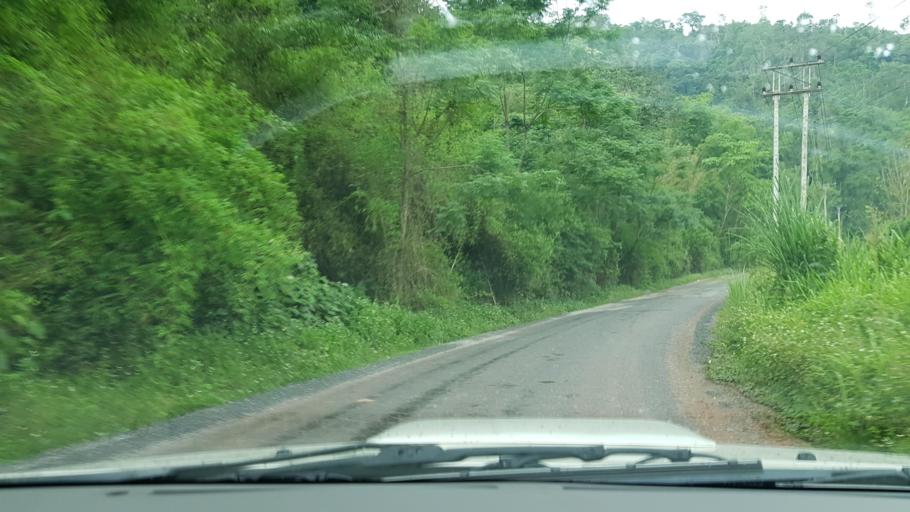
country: LA
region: Oudomxai
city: Muang Xay
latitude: 20.6302
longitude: 101.9632
